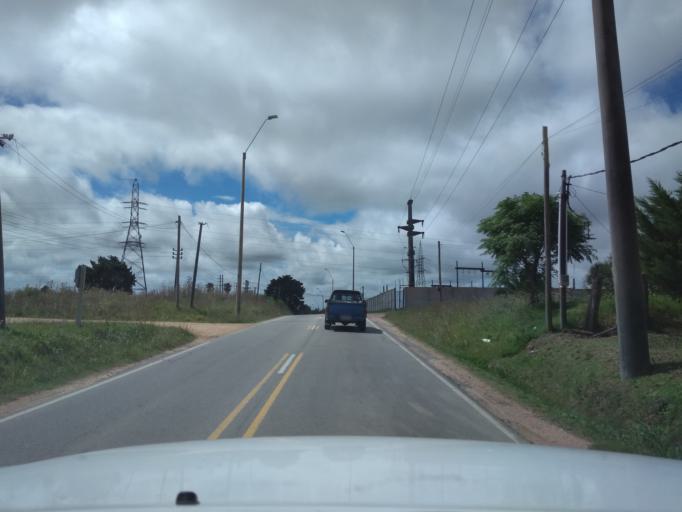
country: UY
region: Canelones
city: Pando
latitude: -34.7005
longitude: -55.9663
